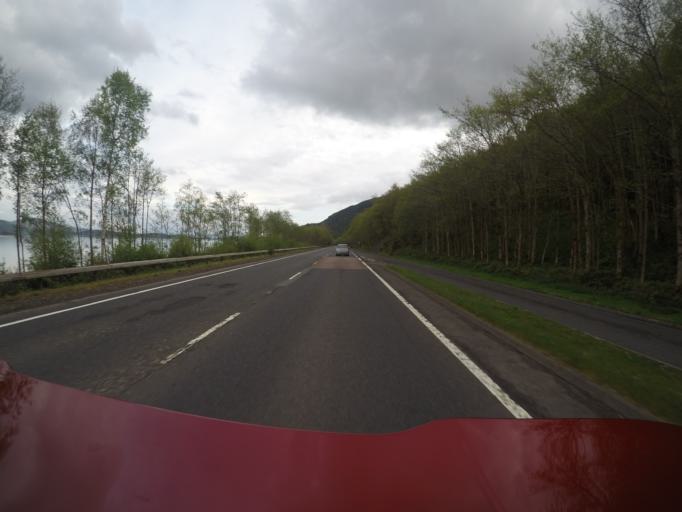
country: GB
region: Scotland
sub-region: Argyll and Bute
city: Helensburgh
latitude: 56.1268
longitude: -4.6539
